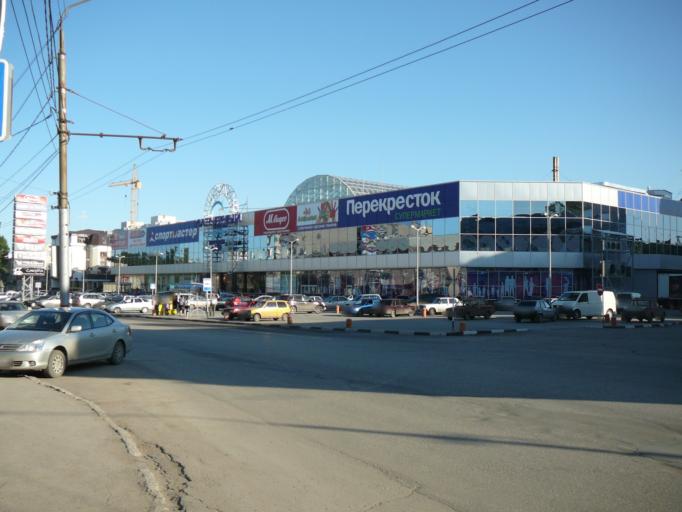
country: RU
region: Saratov
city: Engel's
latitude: 51.5038
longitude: 46.1180
